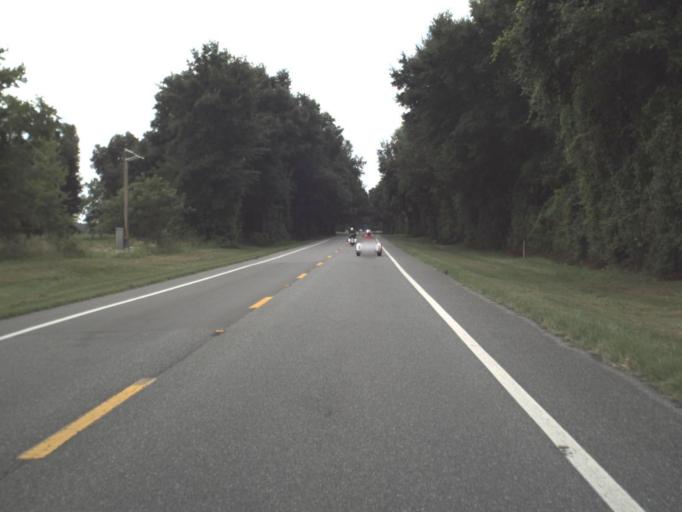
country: US
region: Florida
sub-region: Alachua County
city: Newberry
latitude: 29.6144
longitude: -82.5916
